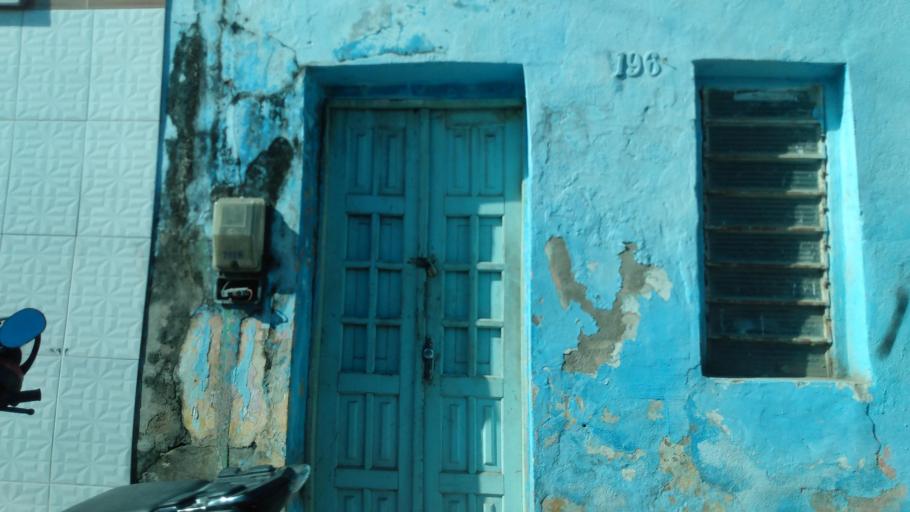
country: ET
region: Oromiya
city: Gore
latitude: 8.2000
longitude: 35.5674
